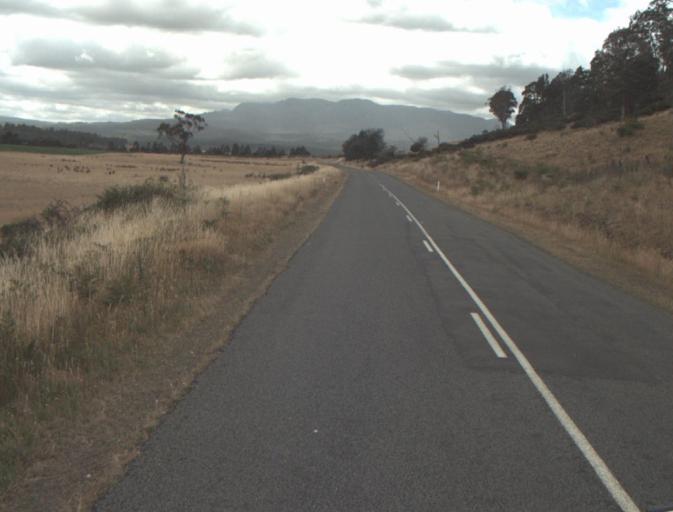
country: AU
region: Tasmania
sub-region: Northern Midlands
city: Evandale
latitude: -41.4935
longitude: 147.4336
